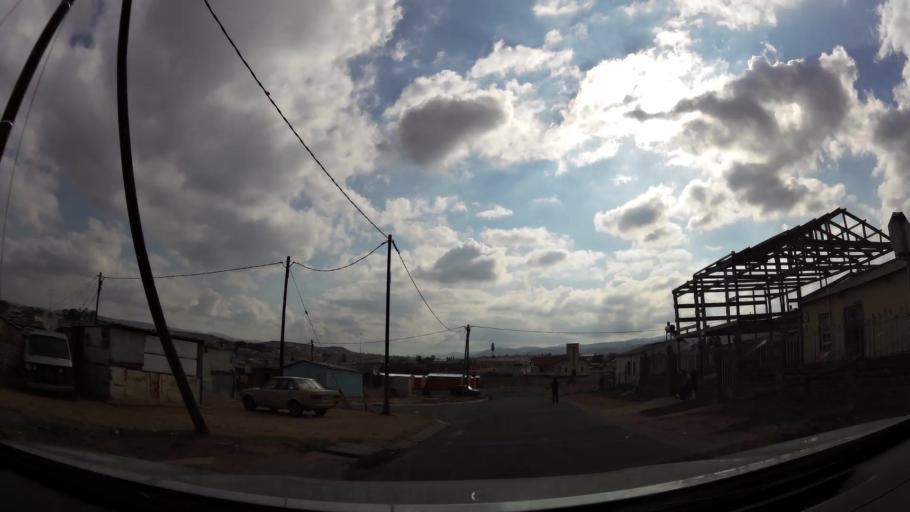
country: ZA
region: Eastern Cape
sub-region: Nelson Mandela Bay Metropolitan Municipality
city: Uitenhage
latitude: -33.7482
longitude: 25.3924
